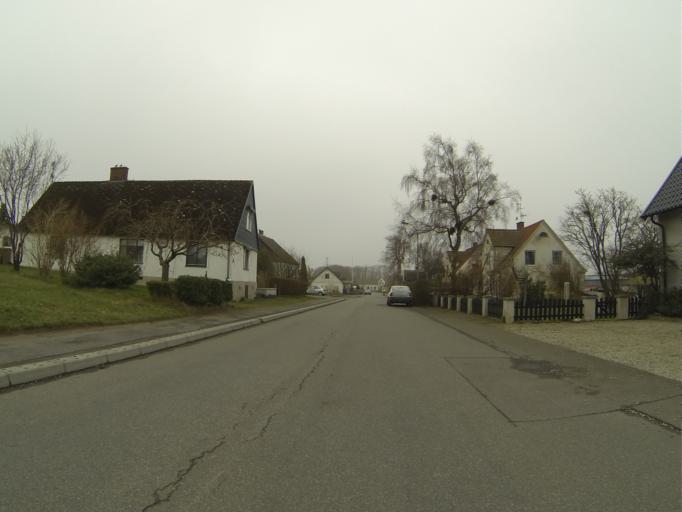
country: SE
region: Skane
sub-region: Simrishamns Kommun
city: Kivik
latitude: 55.5484
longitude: 14.1791
